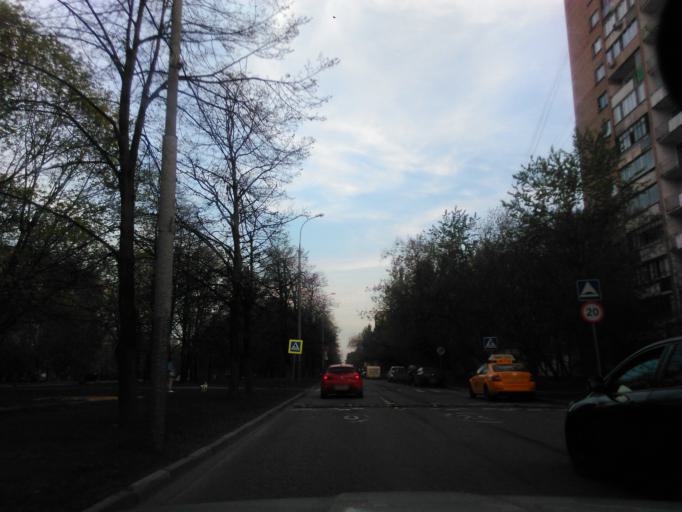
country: RU
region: Moscow
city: Novyye Kuz'minki
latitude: 55.7037
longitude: 37.7481
